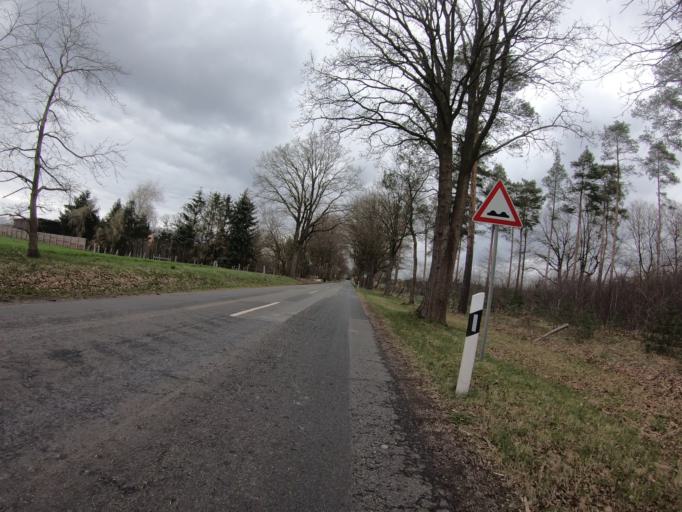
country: DE
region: Lower Saxony
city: Leiferde
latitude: 52.4938
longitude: 10.4368
